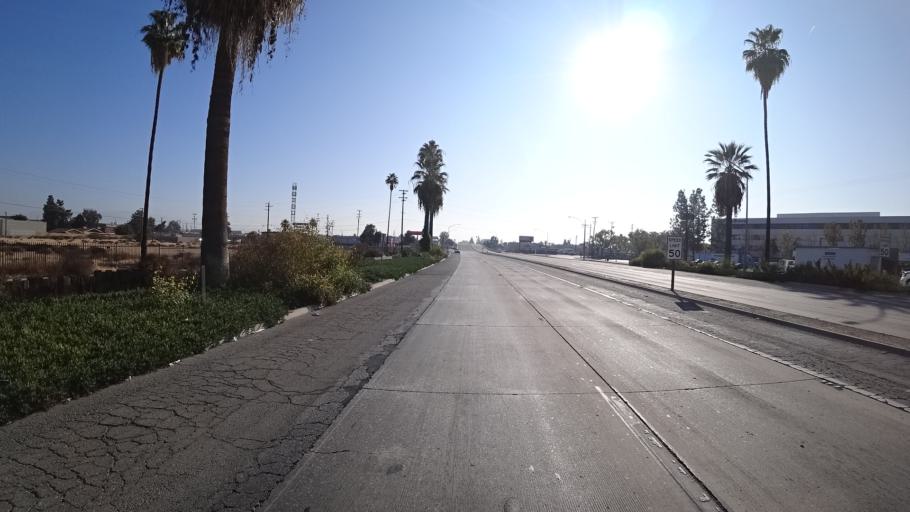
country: US
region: California
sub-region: Kern County
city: Bakersfield
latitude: 35.3891
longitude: -119.0223
